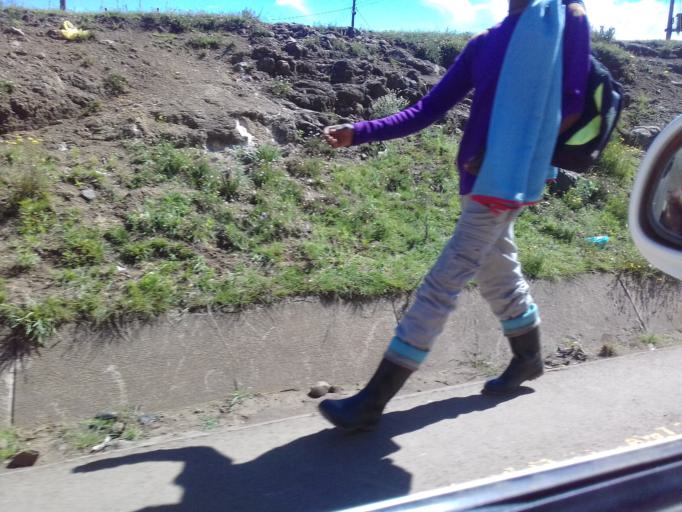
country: LS
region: Thaba-Tseka
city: Thaba-Tseka
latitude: -29.5153
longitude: 28.5949
